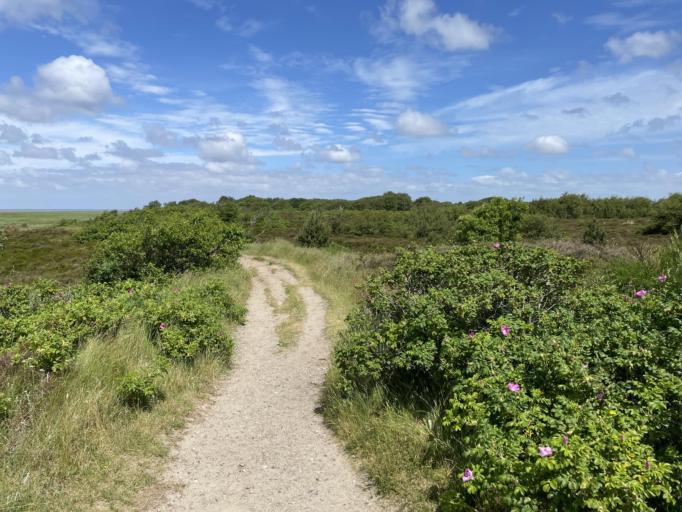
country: DE
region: Lower Saxony
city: Nordholz
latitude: 53.8688
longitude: 8.6038
